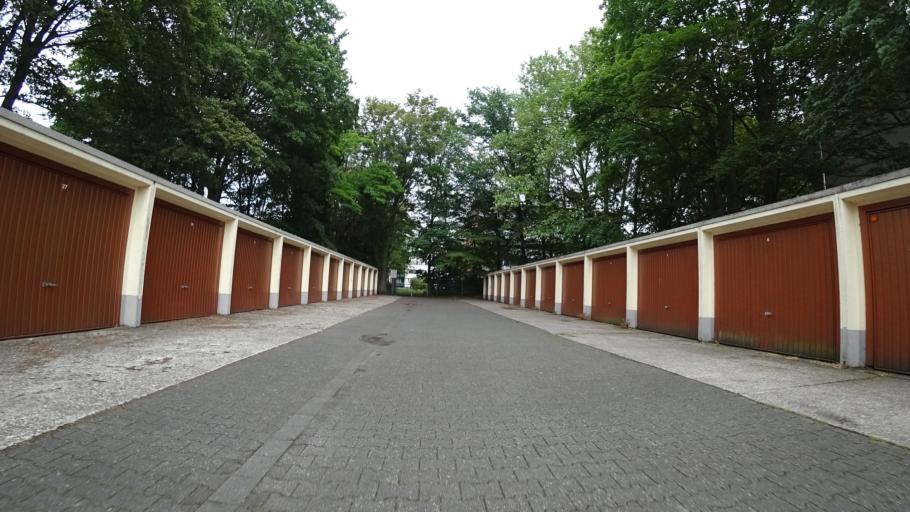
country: DE
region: North Rhine-Westphalia
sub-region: Regierungsbezirk Detmold
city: Guetersloh
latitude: 51.9326
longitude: 8.3657
